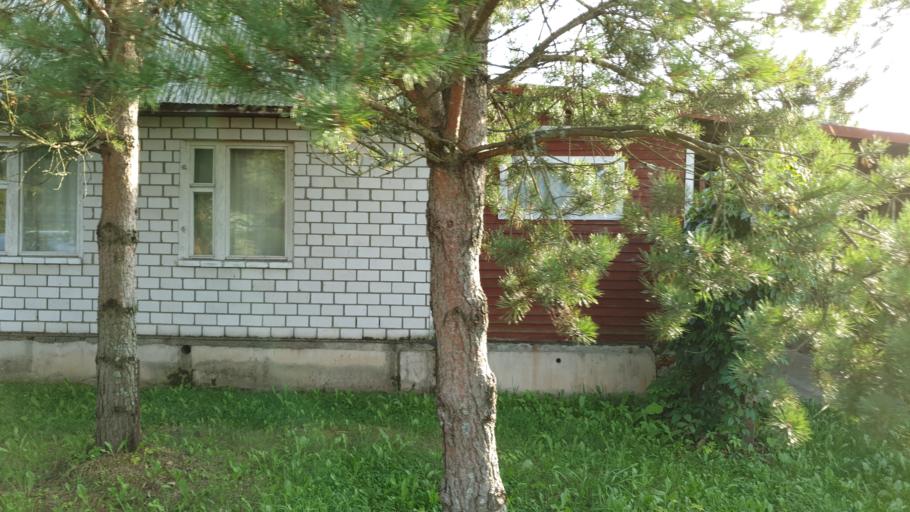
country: RU
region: Leningrad
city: Ivangorod
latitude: 59.4251
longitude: 28.3292
